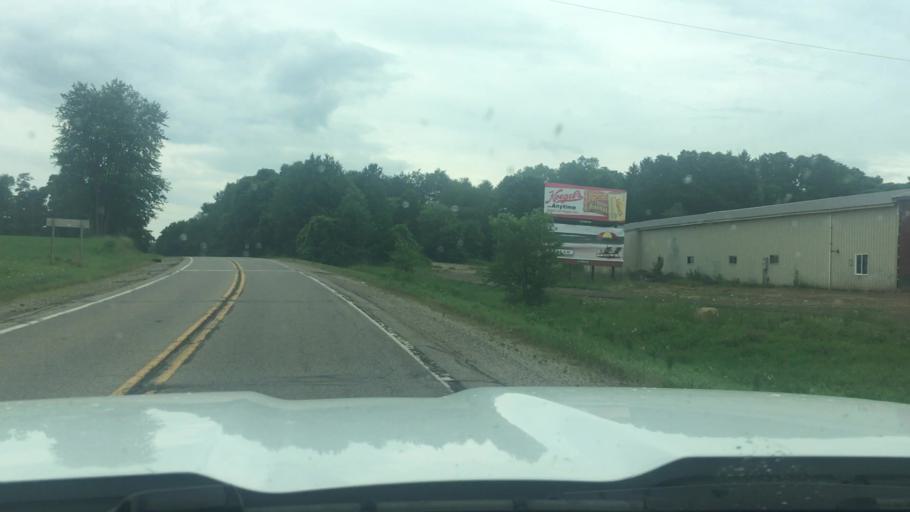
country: US
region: Michigan
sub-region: Ionia County
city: Ionia
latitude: 42.9867
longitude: -85.0900
